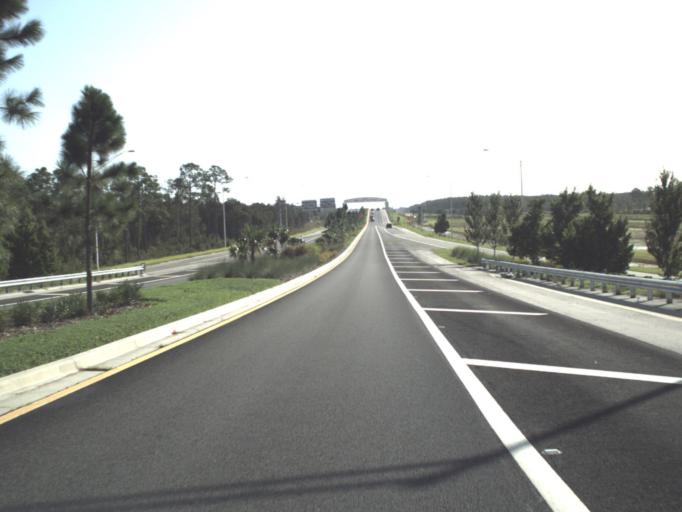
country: US
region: Florida
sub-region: Lee County
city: Three Oaks
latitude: 26.5117
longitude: -81.7927
